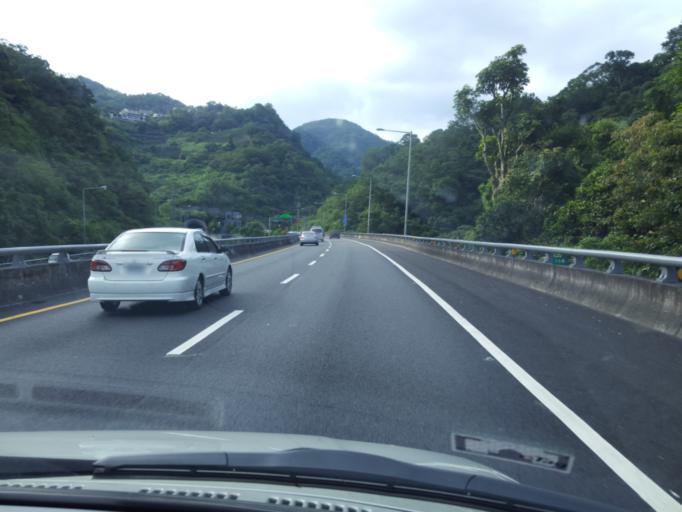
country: TW
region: Taiwan
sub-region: Keelung
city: Keelung
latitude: 24.9483
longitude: 121.7043
